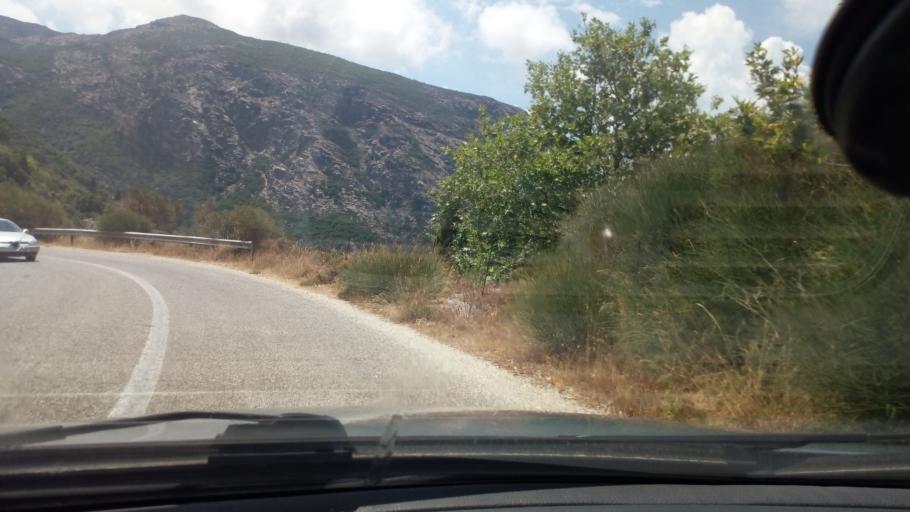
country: GR
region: North Aegean
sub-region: Nomos Samou
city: Agios Kirykos
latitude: 37.6433
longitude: 26.2605
